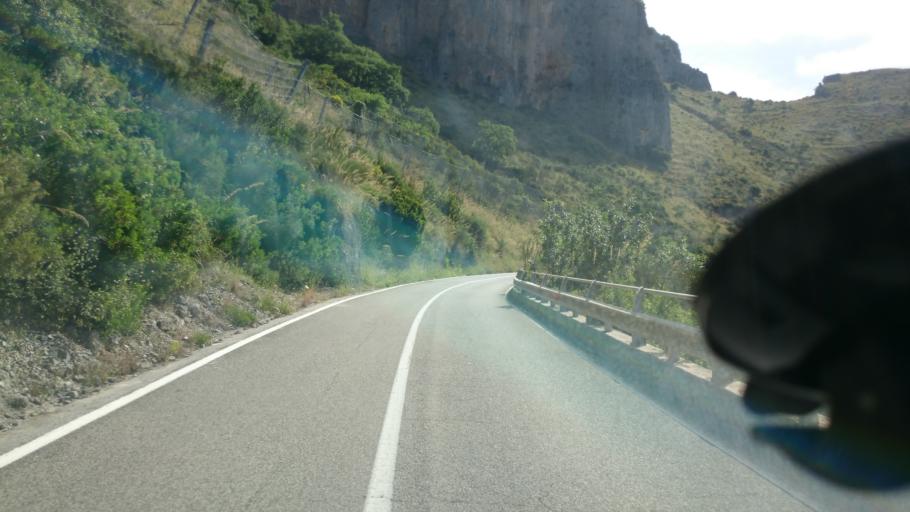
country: IT
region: Campania
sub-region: Provincia di Salerno
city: Sapri
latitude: 40.0427
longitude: 15.6540
